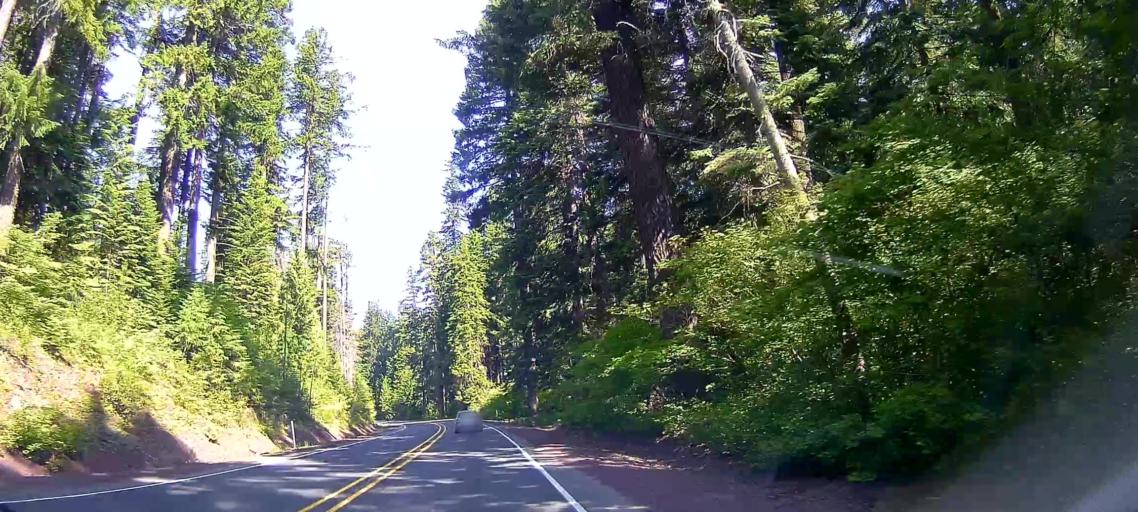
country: US
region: Oregon
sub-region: Jefferson County
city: Warm Springs
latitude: 45.1122
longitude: -121.5663
